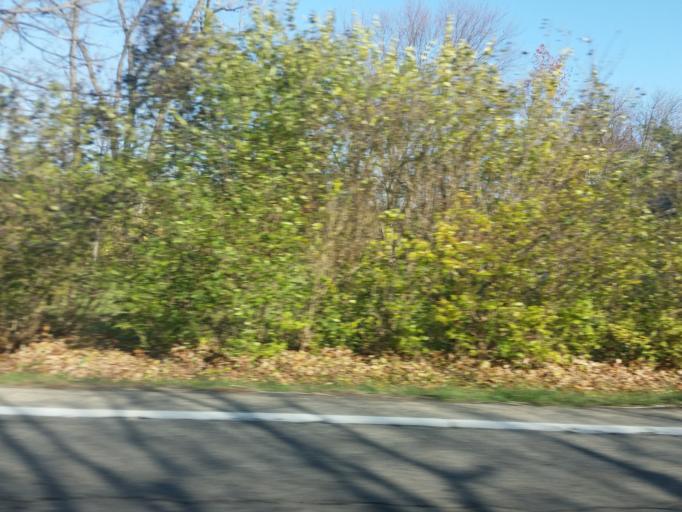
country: US
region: Ohio
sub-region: Butler County
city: Oxford
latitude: 39.4737
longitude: -84.7069
